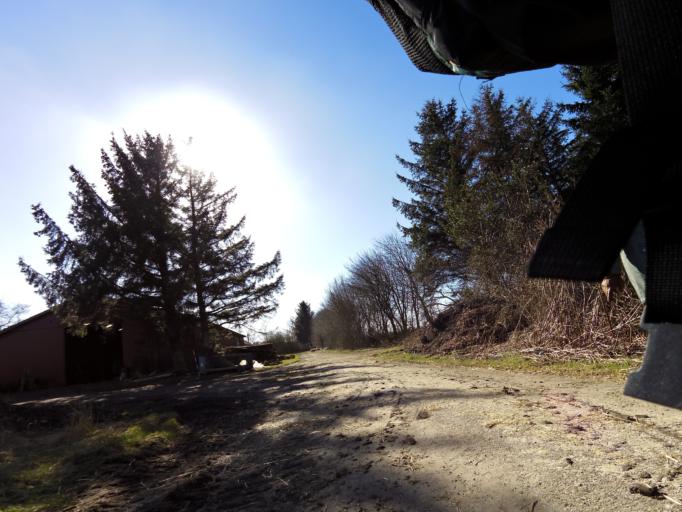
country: DK
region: South Denmark
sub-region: Varde Kommune
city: Varde
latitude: 55.5781
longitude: 8.4054
